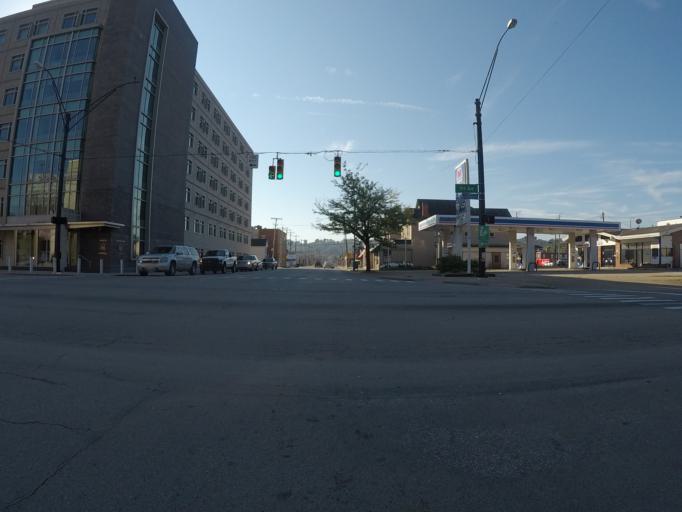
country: US
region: West Virginia
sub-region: Cabell County
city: Huntington
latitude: 38.4192
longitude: -82.4453
